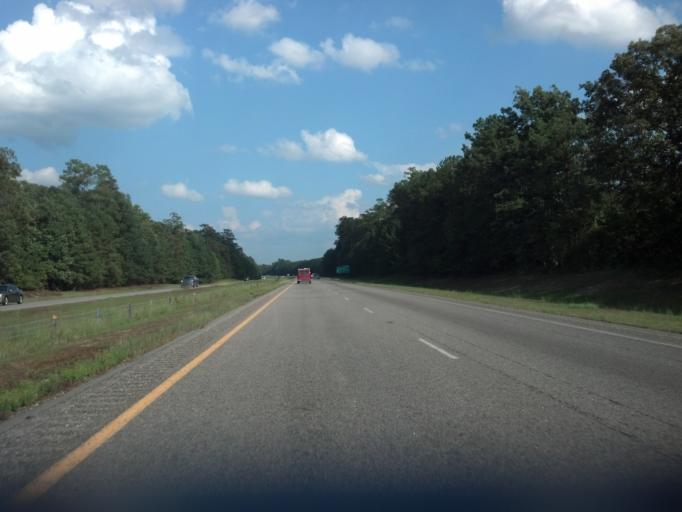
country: US
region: North Carolina
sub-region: Edgecombe County
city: Tarboro
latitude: 35.8914
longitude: -77.6145
